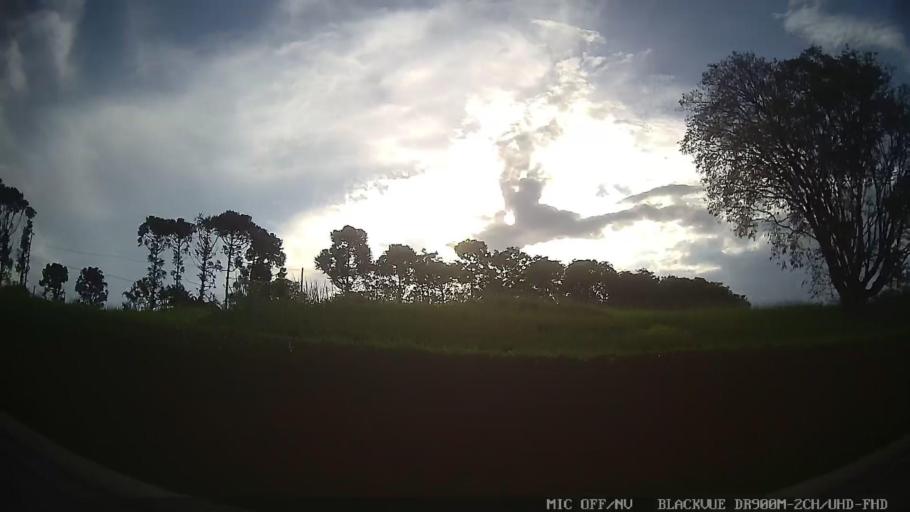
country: BR
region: Sao Paulo
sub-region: Tiete
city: Tiete
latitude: -23.1227
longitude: -47.6997
